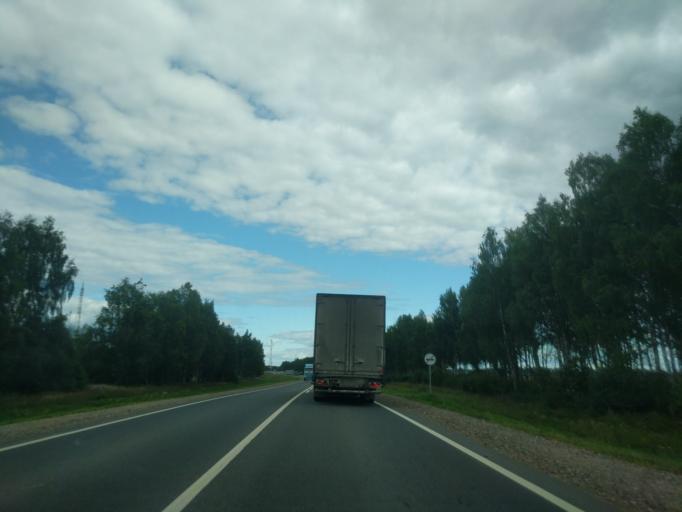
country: RU
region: Kostroma
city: Ostrovskoye
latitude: 57.8147
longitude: 42.2185
